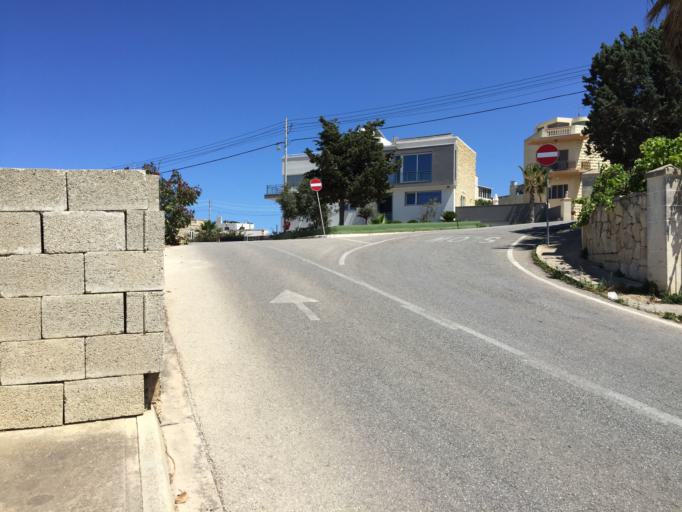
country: MT
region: Is-Swieqi
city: Swieqi
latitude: 35.9147
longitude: 14.4803
